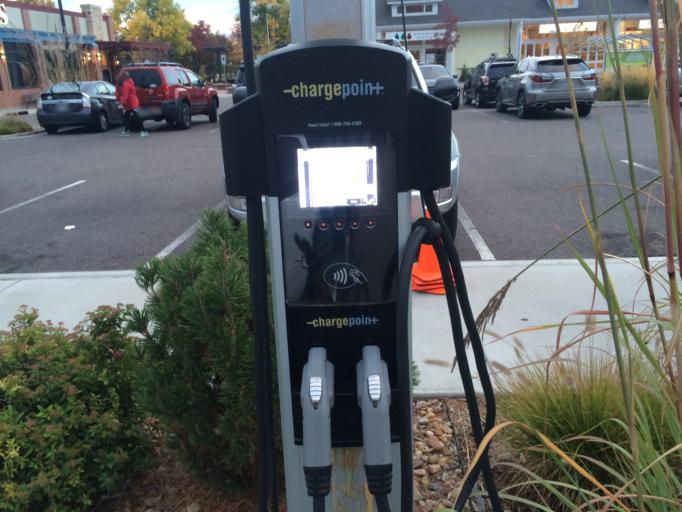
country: US
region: Colorado
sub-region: Boulder County
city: Louisville
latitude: 39.9877
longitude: -105.1344
